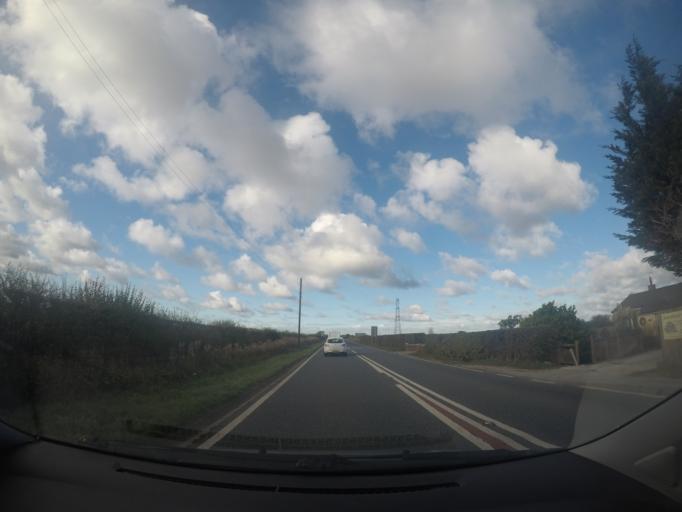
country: GB
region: England
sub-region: City of York
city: Nether Poppleton
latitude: 53.9874
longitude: -1.2226
